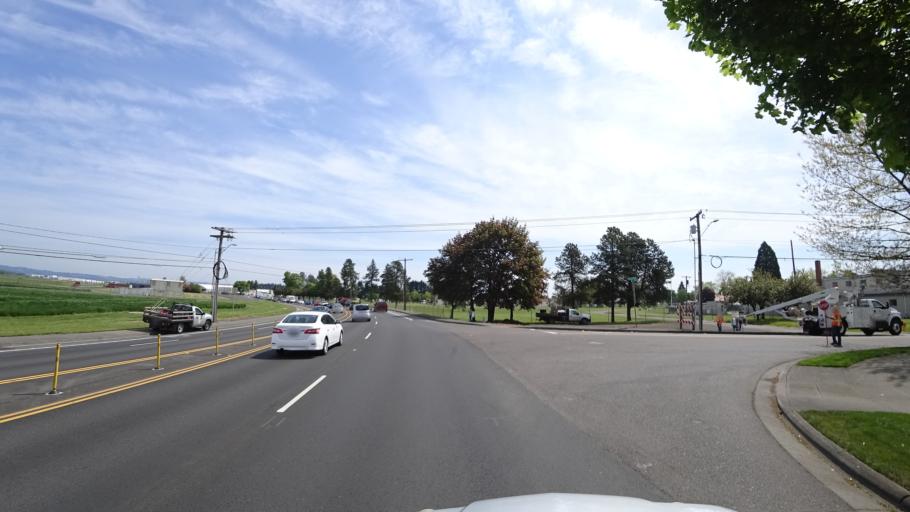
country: US
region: Oregon
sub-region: Washington County
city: Hillsboro
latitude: 45.5306
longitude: -122.9542
